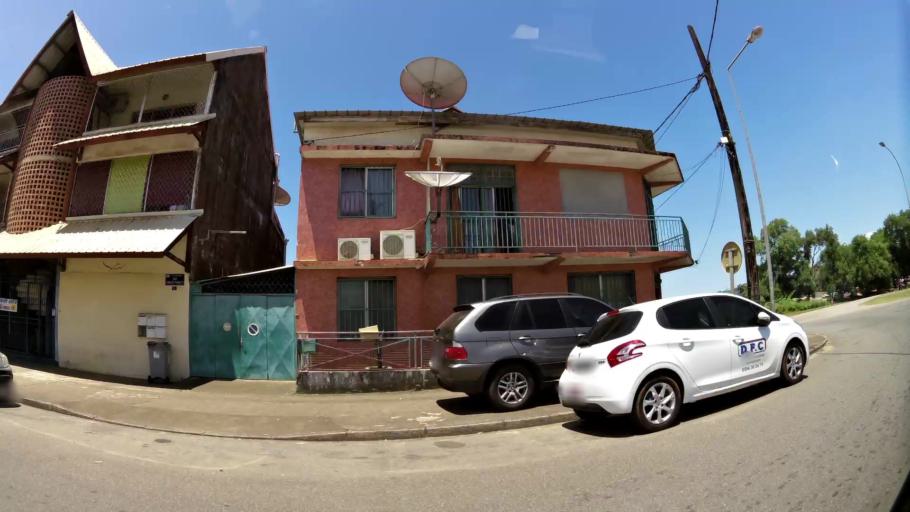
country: GF
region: Guyane
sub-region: Guyane
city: Cayenne
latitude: 4.9311
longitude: -52.3324
